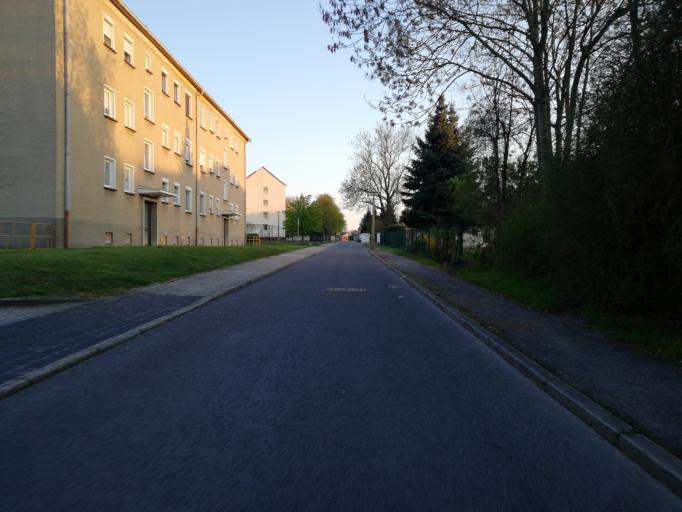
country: DE
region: Brandenburg
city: Calau
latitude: 51.7449
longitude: 13.9518
